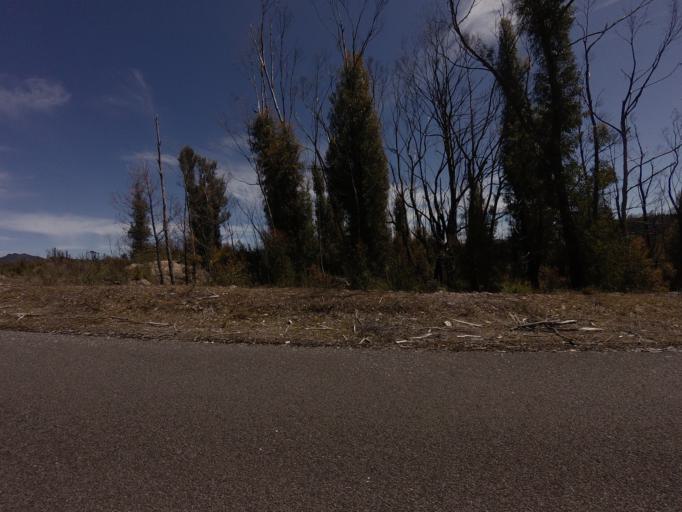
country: AU
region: Tasmania
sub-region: Huon Valley
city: Geeveston
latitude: -42.8509
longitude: 146.2352
